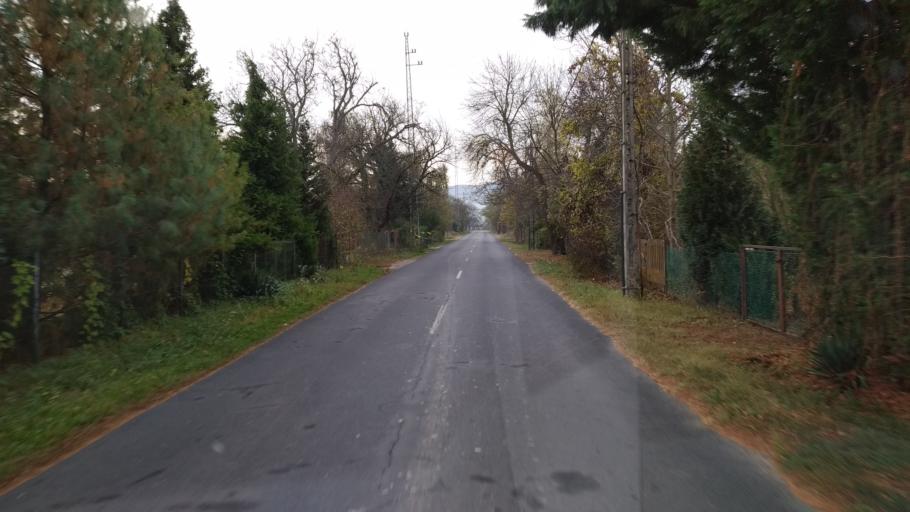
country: HU
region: Pest
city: Tahitotfalu
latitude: 47.7724
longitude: 19.0891
